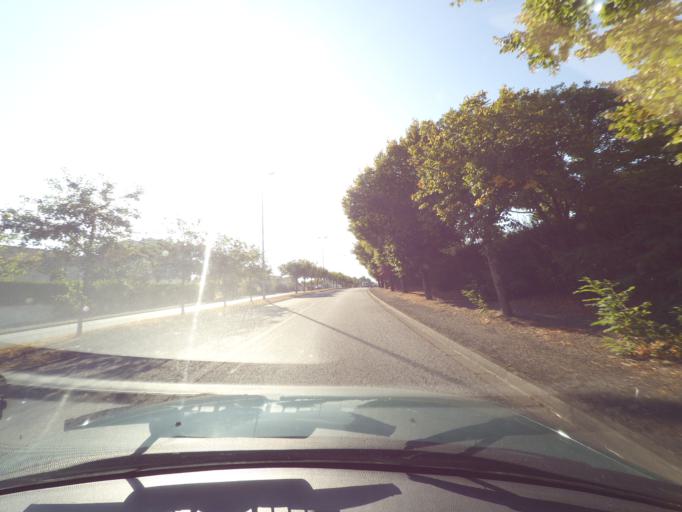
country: FR
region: Poitou-Charentes
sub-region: Departement des Deux-Sevres
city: Chatillon-sur-Thouet
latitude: 46.6532
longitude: -0.2309
